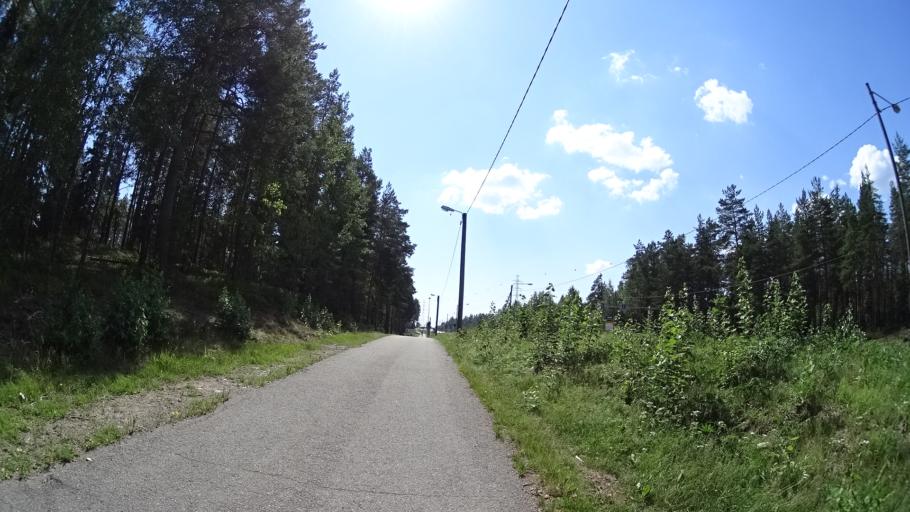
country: FI
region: Uusimaa
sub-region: Helsinki
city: Vantaa
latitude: 60.3171
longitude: 25.0001
